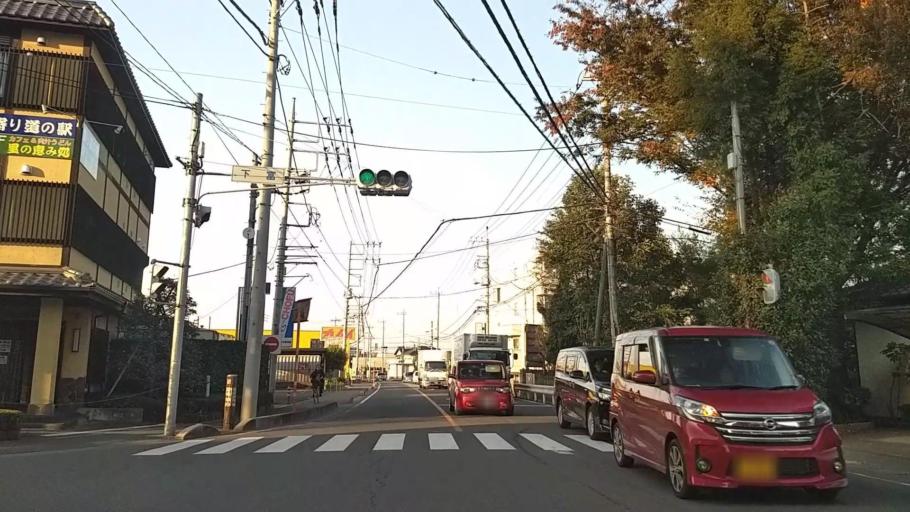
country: JP
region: Saitama
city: Tokorozawa
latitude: 35.8273
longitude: 139.4658
